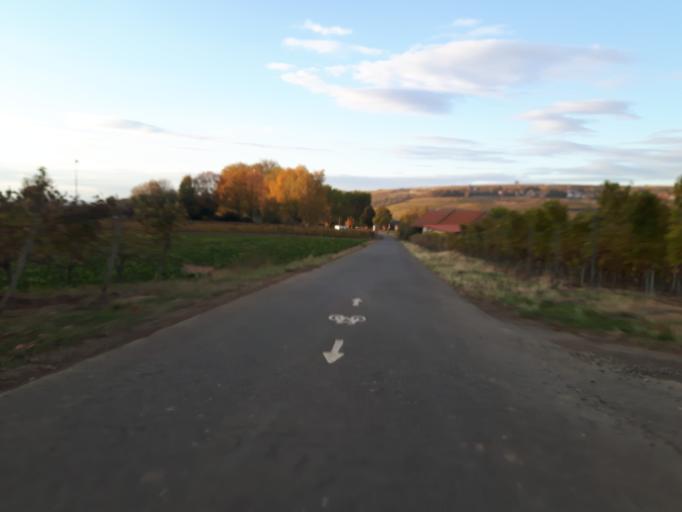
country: DE
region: Rheinland-Pfalz
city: Molsheim
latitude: 49.6329
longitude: 8.1755
